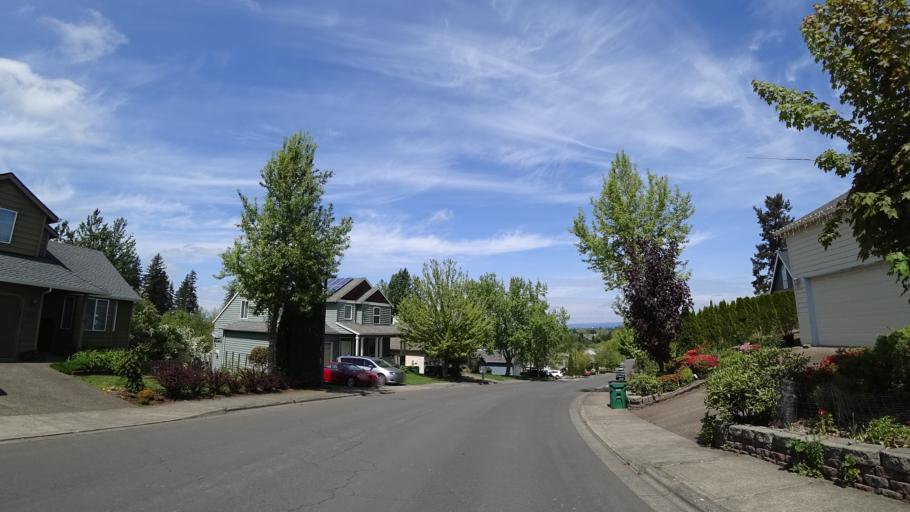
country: US
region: Oregon
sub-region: Washington County
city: Aloha
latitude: 45.4653
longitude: -122.8897
